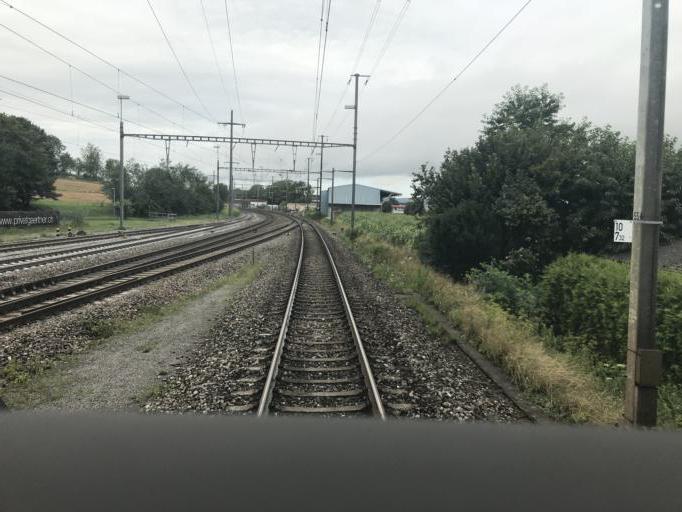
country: CH
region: Zurich
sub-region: Bezirk Dielsdorf
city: Rumlang
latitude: 47.4556
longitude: 8.5312
